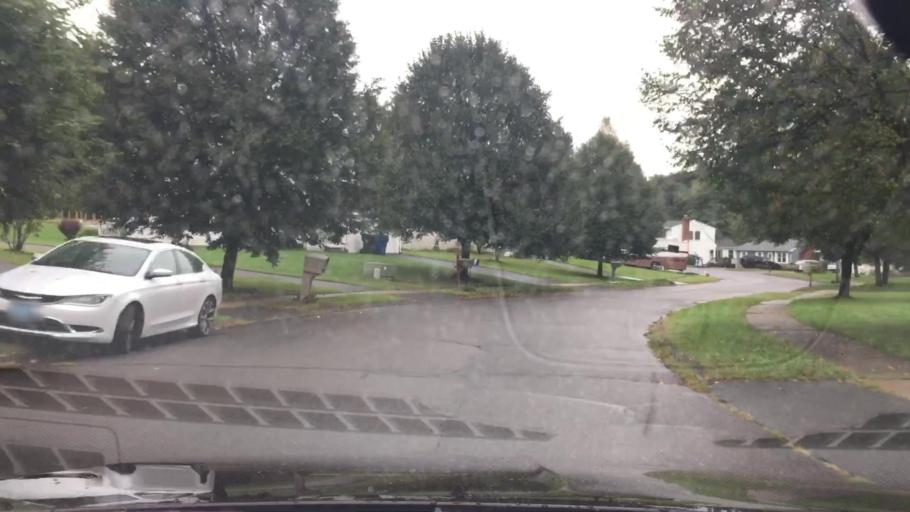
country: US
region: Connecticut
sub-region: Hartford County
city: Kensington
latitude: 41.6160
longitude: -72.7140
